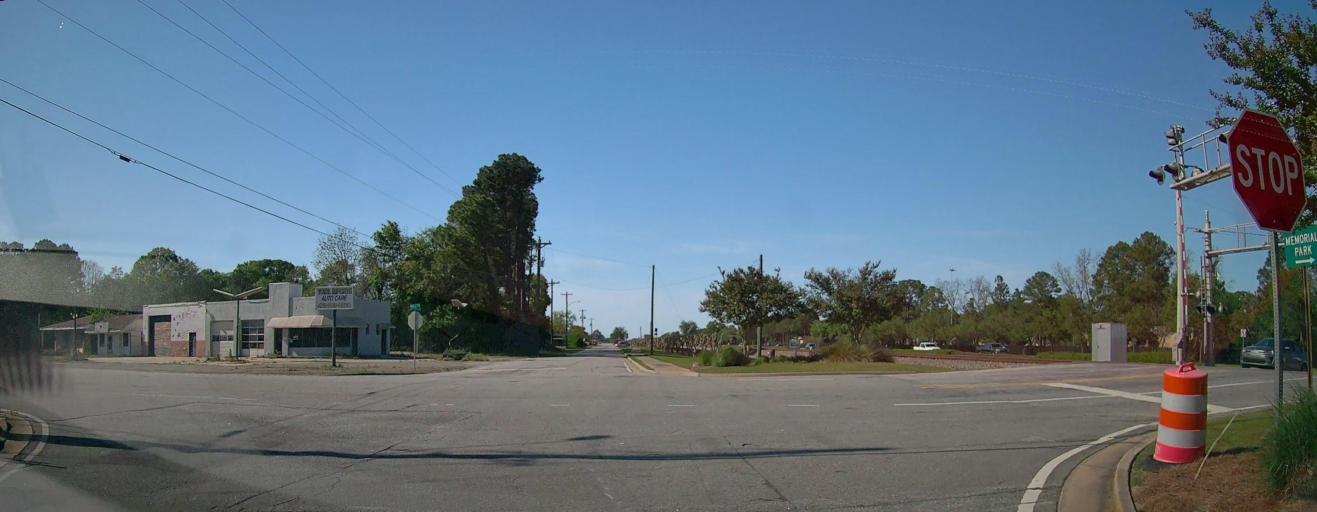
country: US
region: Georgia
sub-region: Houston County
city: Warner Robins
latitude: 32.6122
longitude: -83.5976
